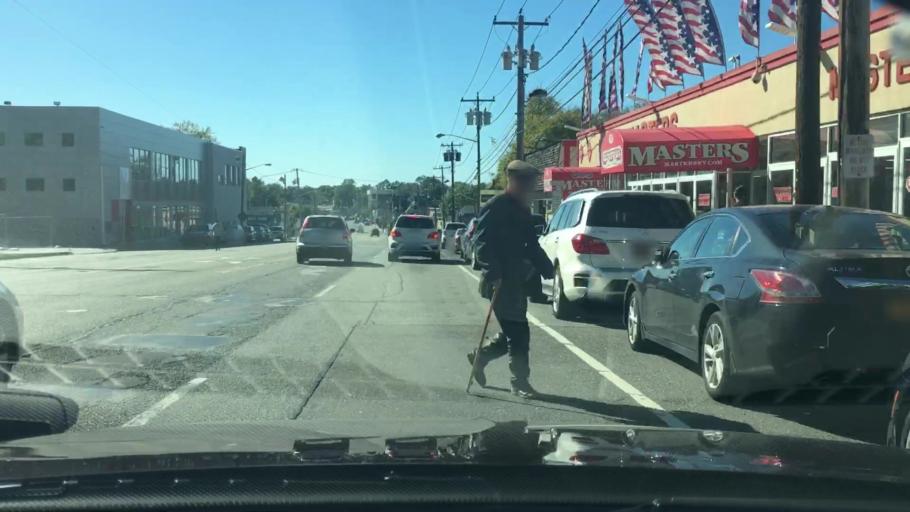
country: US
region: New York
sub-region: Nassau County
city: University Gardens
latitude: 40.7776
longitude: -73.7267
